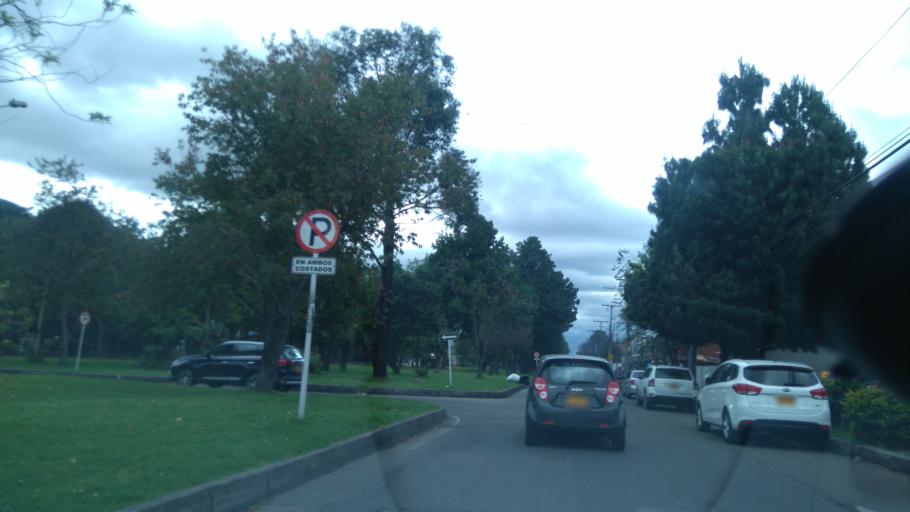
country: CO
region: Bogota D.C.
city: Bogota
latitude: 4.6439
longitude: -74.0913
